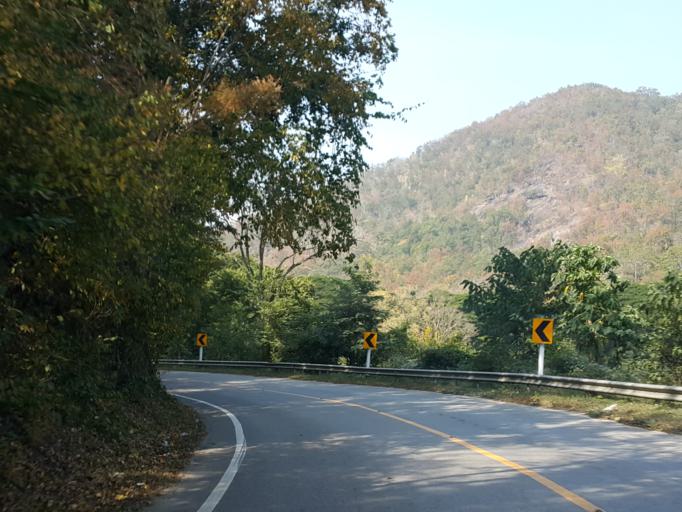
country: TH
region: Chiang Mai
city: Hot
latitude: 18.2223
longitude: 98.4721
